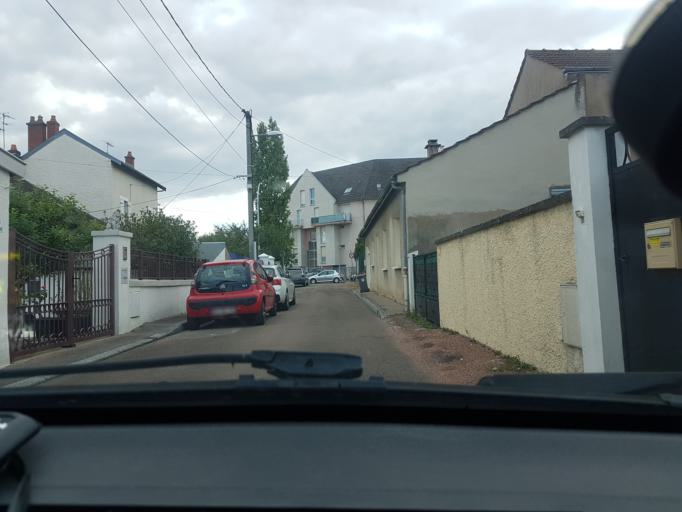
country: FR
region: Bourgogne
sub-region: Departement de la Cote-d'Or
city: Longvic
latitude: 47.3065
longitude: 5.0524
